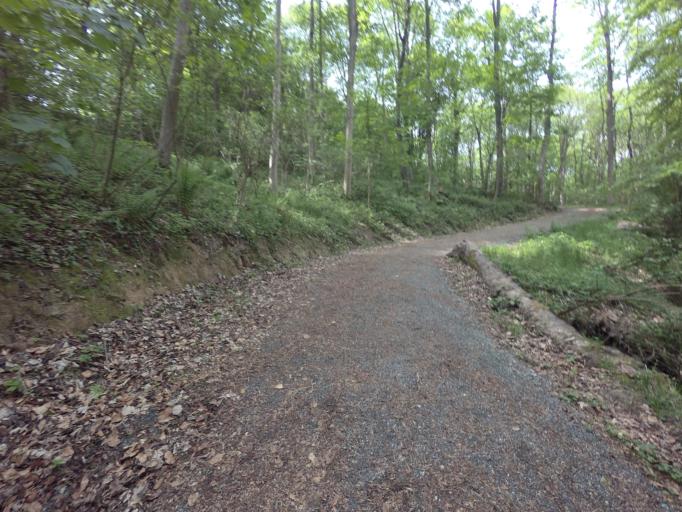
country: DE
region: Lower Saxony
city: Nordstemmen
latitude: 52.1728
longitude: 9.7685
